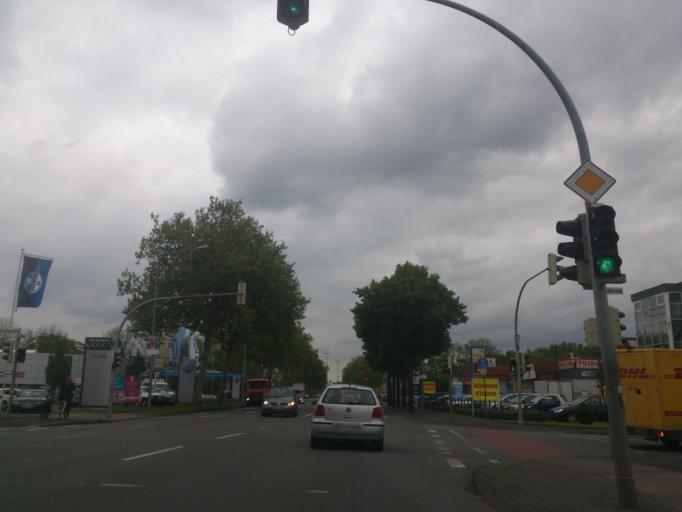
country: DE
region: North Rhine-Westphalia
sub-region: Regierungsbezirk Detmold
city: Paderborn
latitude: 51.7309
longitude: 8.7643
